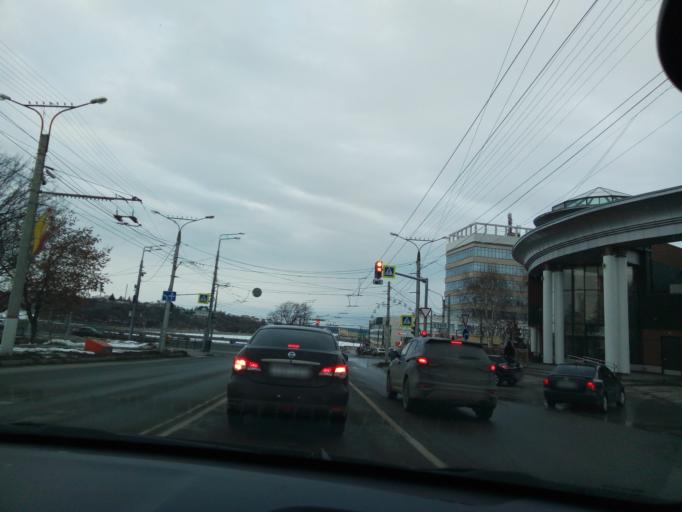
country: RU
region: Chuvashia
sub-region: Cheboksarskiy Rayon
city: Cheboksary
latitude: 56.1434
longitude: 47.2460
